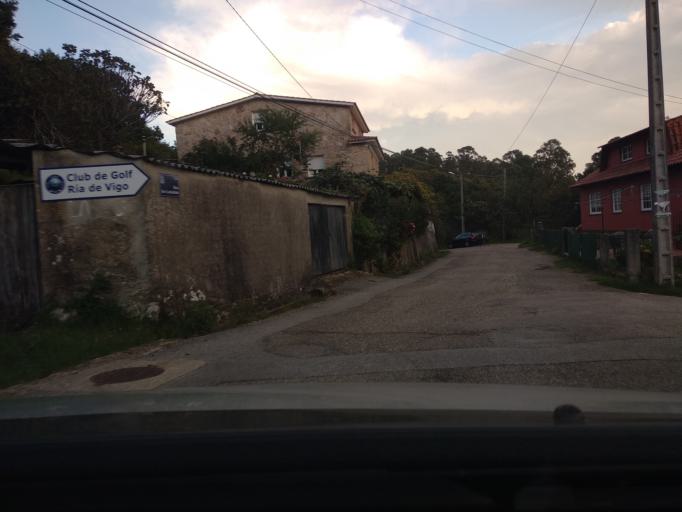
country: ES
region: Galicia
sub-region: Provincia de Pontevedra
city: Moana
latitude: 42.3066
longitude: -8.6983
